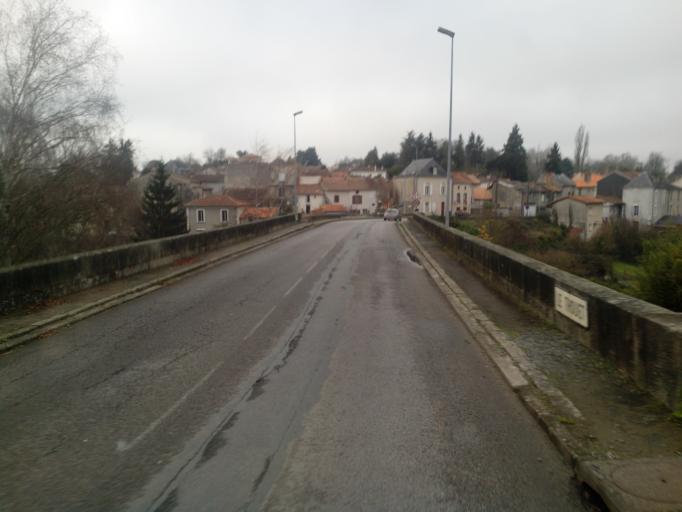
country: FR
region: Poitou-Charentes
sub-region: Departement des Deux-Sevres
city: Parthenay
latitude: 46.6525
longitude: -0.2471
